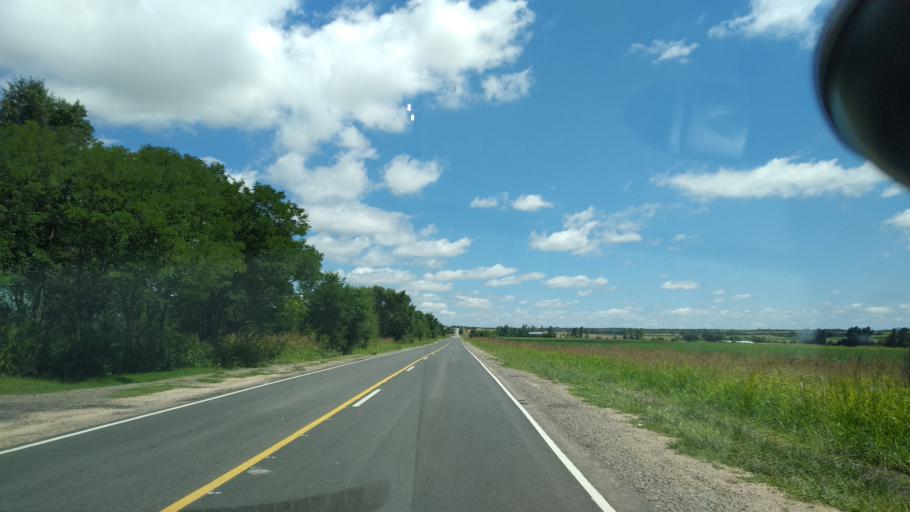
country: AR
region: Cordoba
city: Villa Cura Brochero
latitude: -31.6459
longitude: -65.1012
